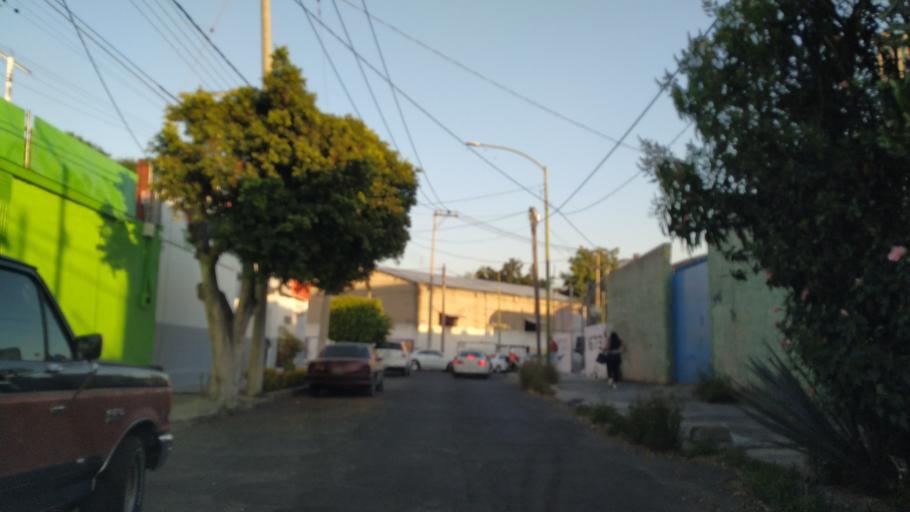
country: MX
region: Jalisco
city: Tlaquepaque
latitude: 20.6515
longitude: -103.3317
